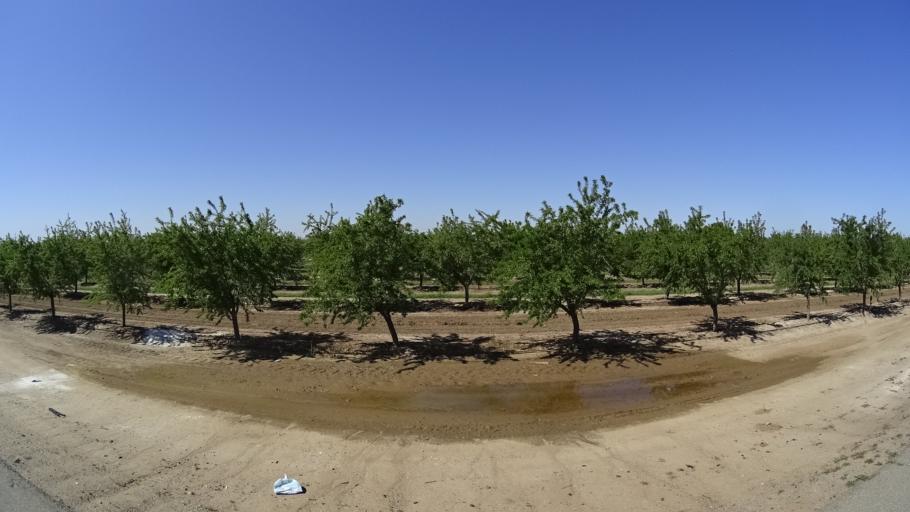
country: US
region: California
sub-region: Fresno County
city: West Park
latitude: 36.7187
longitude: -119.8446
